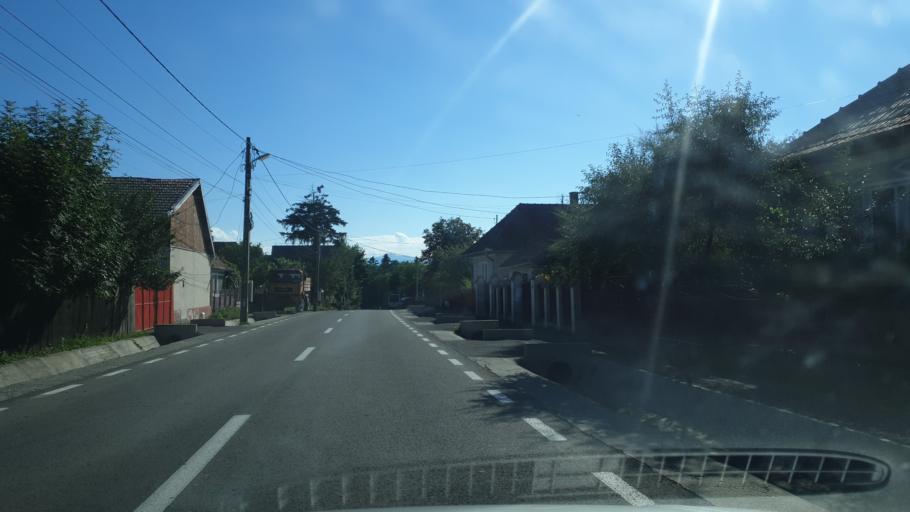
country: RO
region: Covasna
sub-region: Comuna Ilieni
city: Ilieni
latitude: 45.7784
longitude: 25.7537
